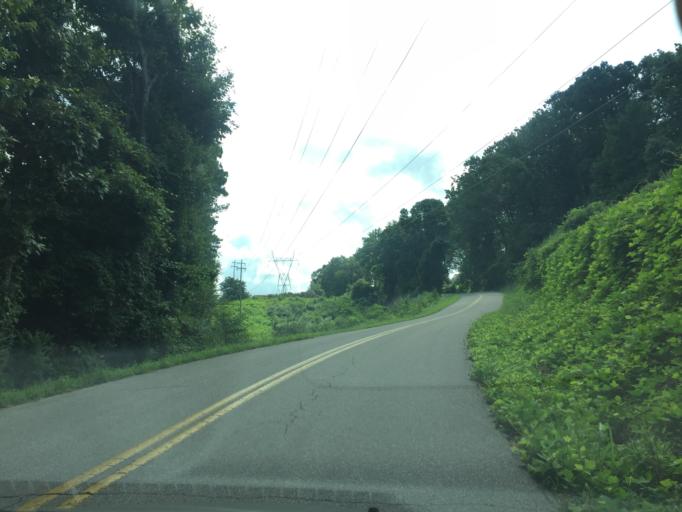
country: US
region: Tennessee
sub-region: Hamilton County
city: East Chattanooga
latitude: 35.0952
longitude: -85.2082
